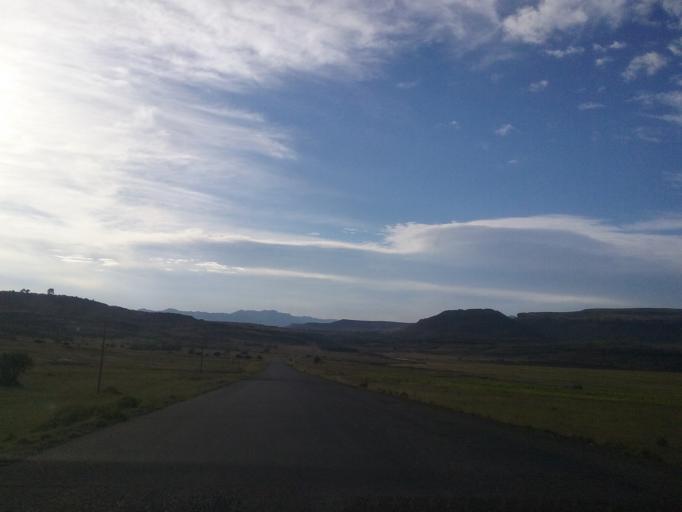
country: LS
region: Quthing
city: Quthing
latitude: -30.3830
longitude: 27.5886
